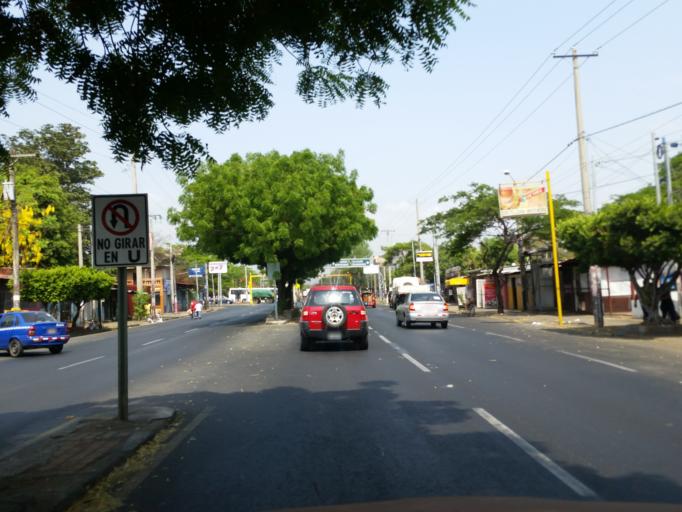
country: NI
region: Managua
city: Managua
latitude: 12.1259
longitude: -86.2943
